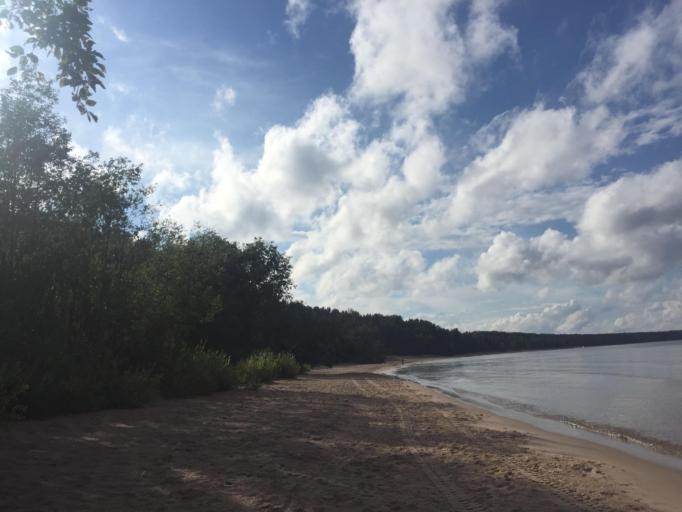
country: RU
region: Leningrad
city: Priozersk
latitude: 60.9740
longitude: 30.2986
